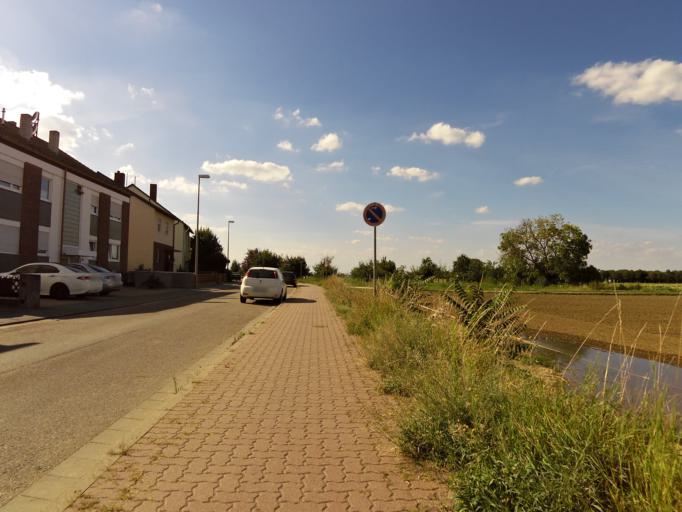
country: DE
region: Rheinland-Pfalz
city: Mutterstadt
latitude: 49.4498
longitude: 8.3572
